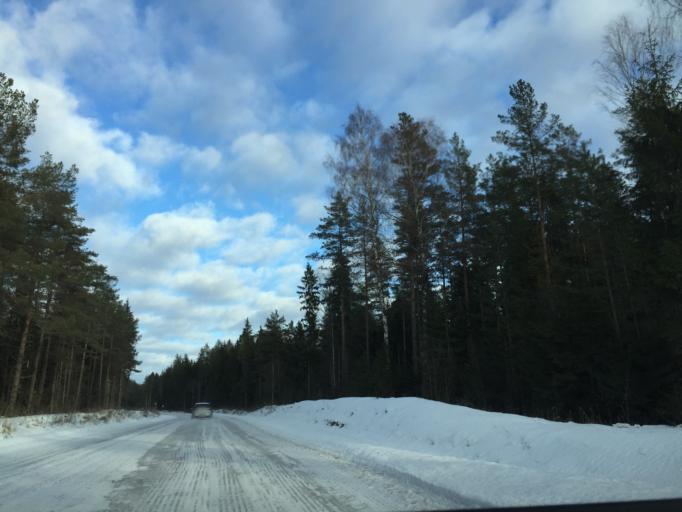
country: LV
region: Ogre
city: Jumprava
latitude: 56.5705
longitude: 24.9344
